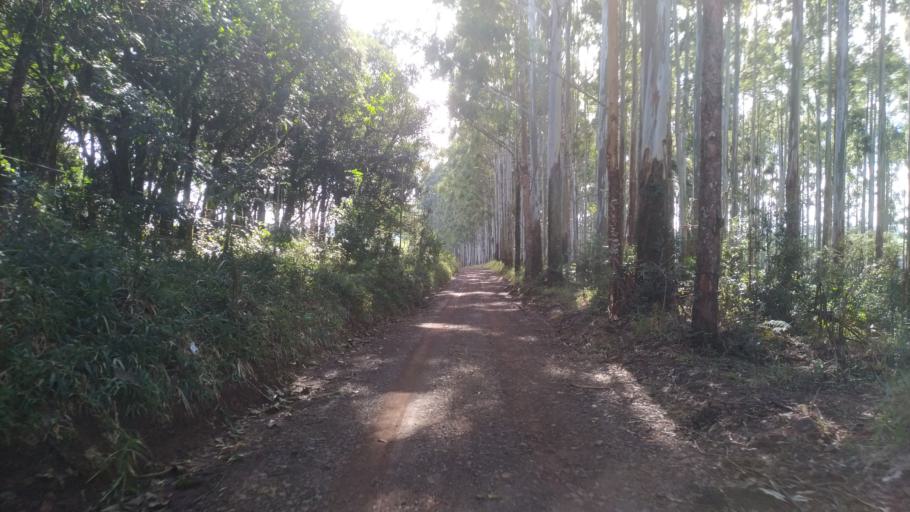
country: BR
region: Santa Catarina
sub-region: Chapeco
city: Chapeco
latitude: -27.1603
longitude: -52.5970
